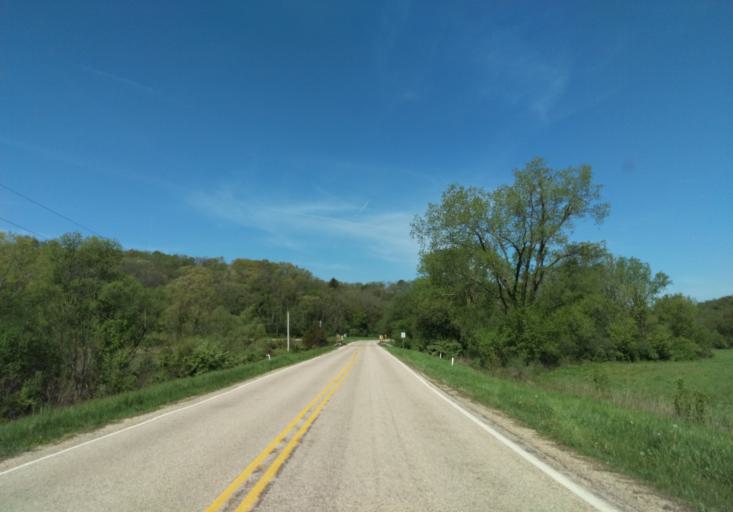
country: US
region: Wisconsin
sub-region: Dane County
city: Mount Horeb
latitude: 43.0590
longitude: -89.7814
